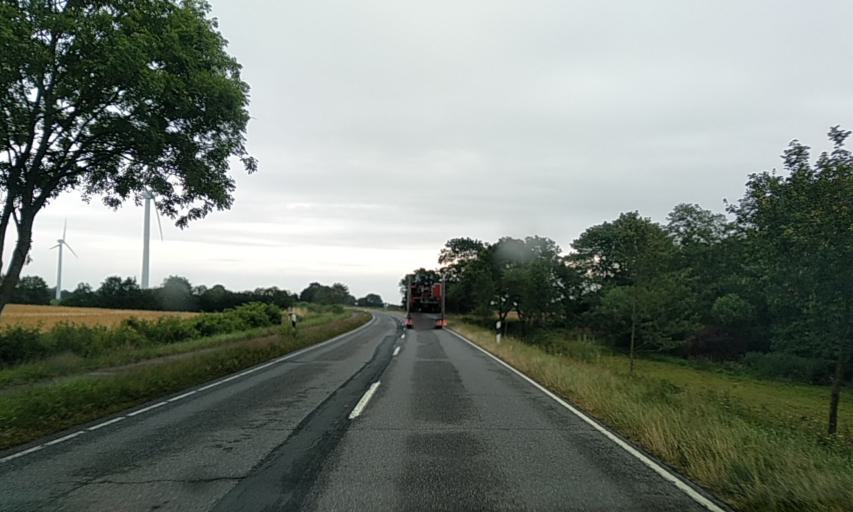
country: DE
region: Schleswig-Holstein
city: Boel
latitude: 54.6403
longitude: 9.7004
